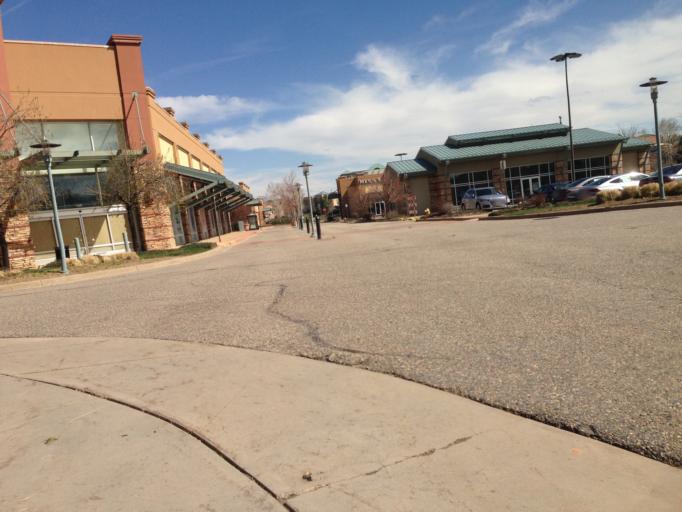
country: US
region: Colorado
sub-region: Broomfield County
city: Broomfield
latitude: 39.9325
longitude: -105.1261
